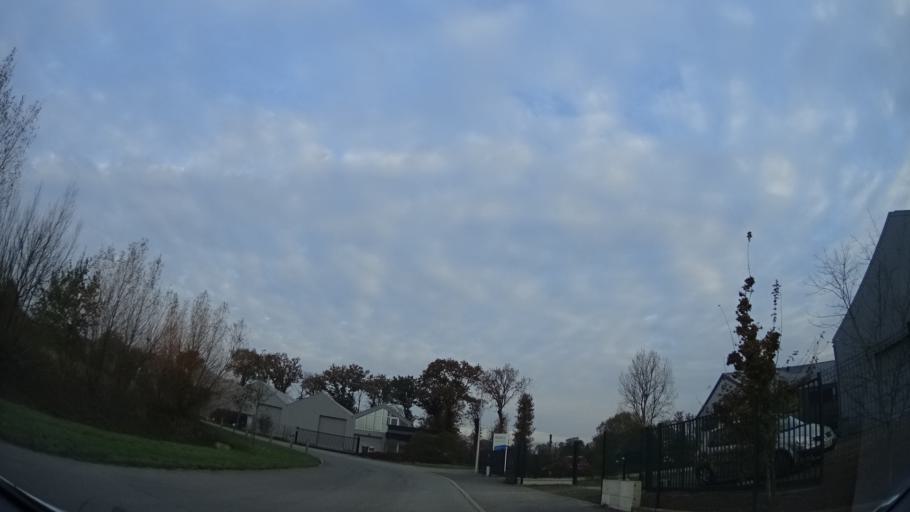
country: FR
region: Brittany
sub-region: Departement d'Ille-et-Vilaine
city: La Chapelle-des-Fougeretz
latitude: 48.1916
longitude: -1.7328
